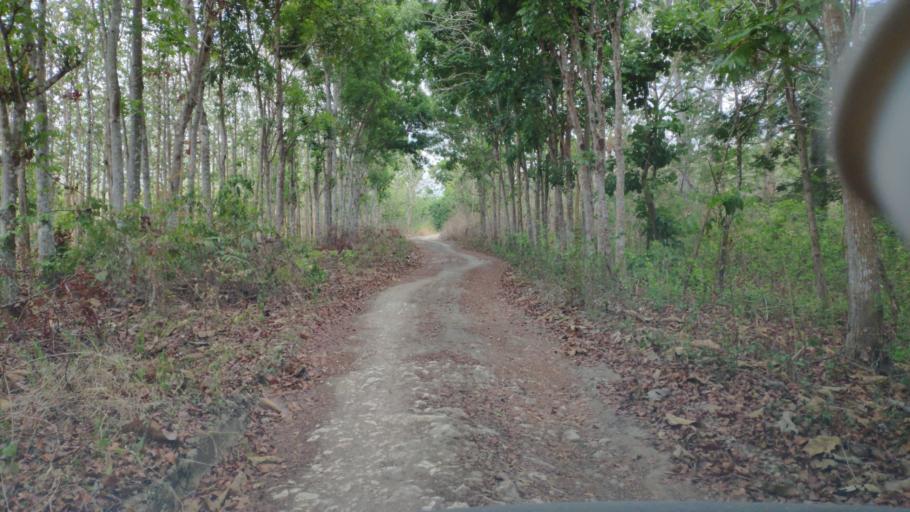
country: ID
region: Central Java
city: Singonegoro
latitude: -6.9906
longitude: 111.5371
